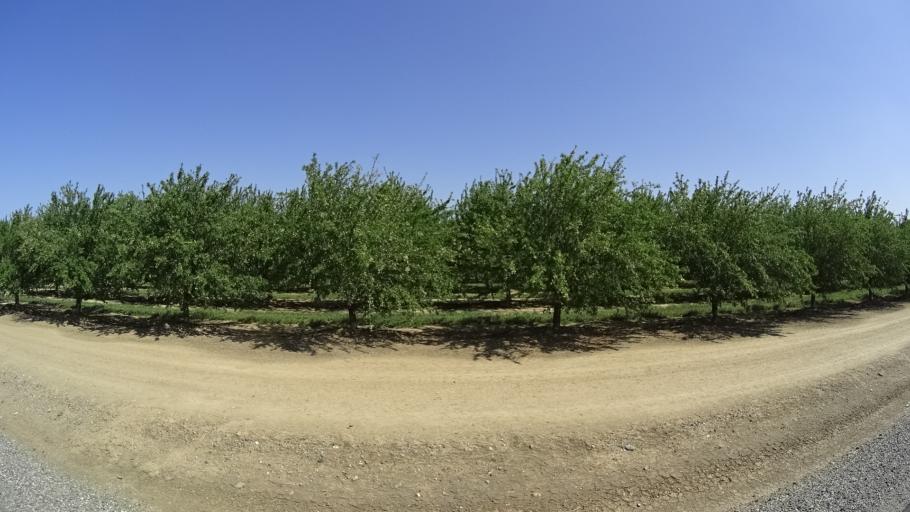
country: US
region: California
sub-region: Glenn County
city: Willows
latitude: 39.6202
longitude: -122.1376
